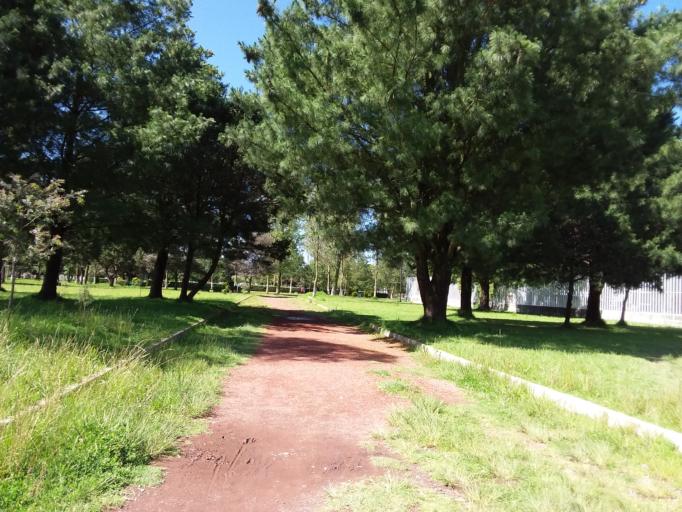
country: MX
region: Mexico
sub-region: Metepec
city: San Salvador Tizatlalli
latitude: 19.2613
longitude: -99.5876
